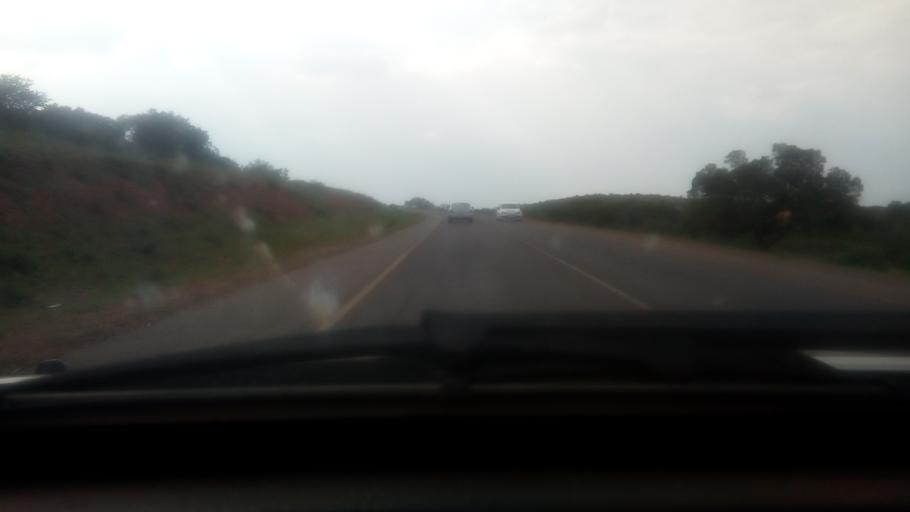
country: BW
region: Kweneng
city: Molepolole
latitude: -24.4128
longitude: 25.6004
